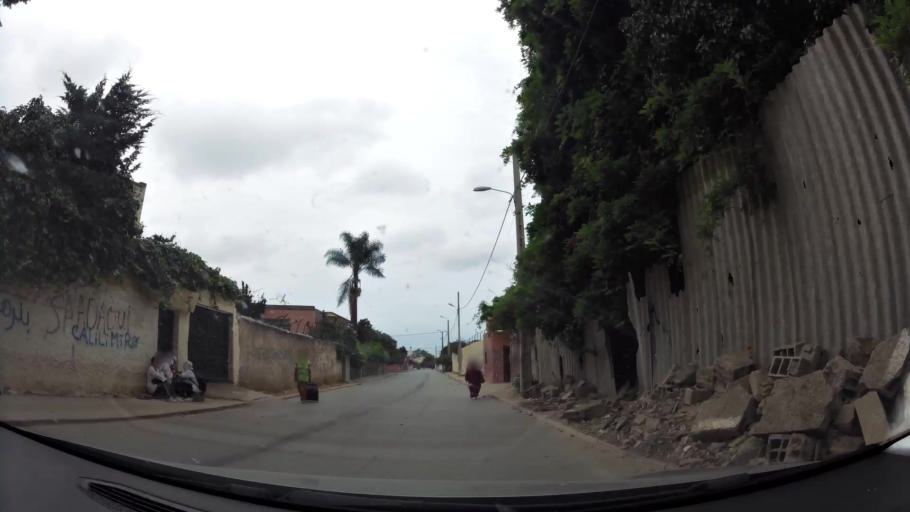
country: MA
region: Rabat-Sale-Zemmour-Zaer
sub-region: Rabat
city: Rabat
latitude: 33.9875
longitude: -6.8209
